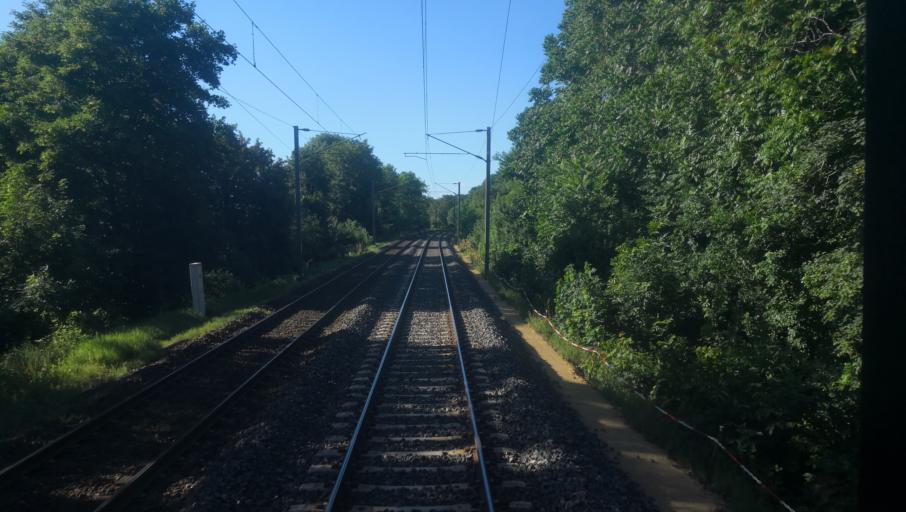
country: FR
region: Centre
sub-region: Departement du Cher
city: Saint-Satur
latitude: 47.3389
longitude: 2.8801
